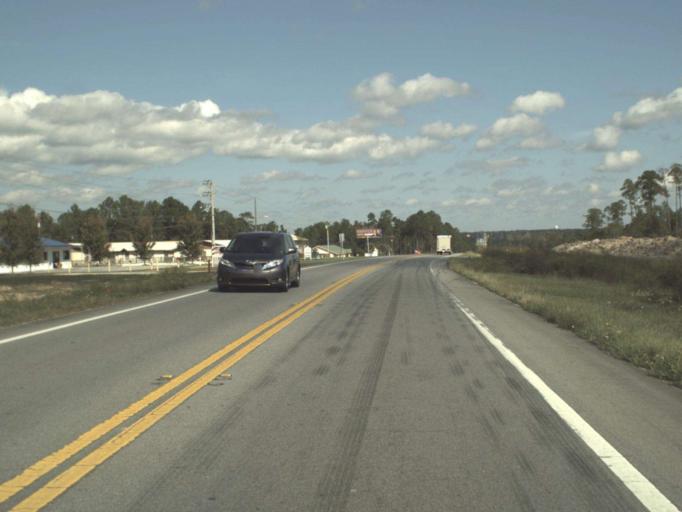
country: US
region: Florida
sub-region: Walton County
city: DeFuniak Springs
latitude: 30.6670
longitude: -86.1228
